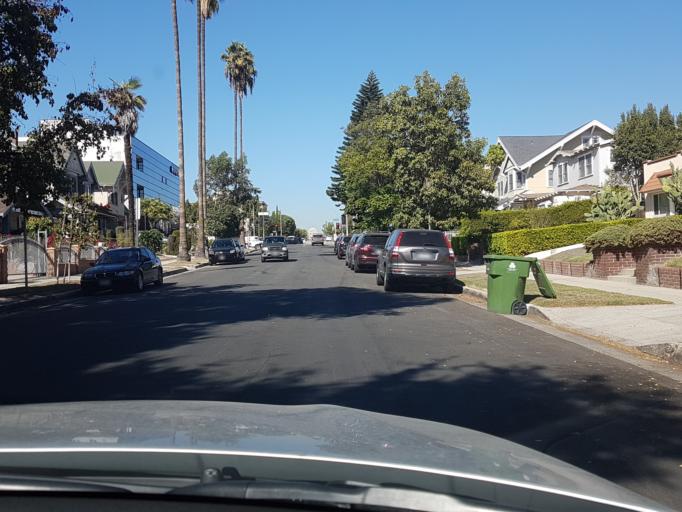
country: US
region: California
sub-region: Los Angeles County
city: Hollywood
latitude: 34.0514
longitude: -118.3112
